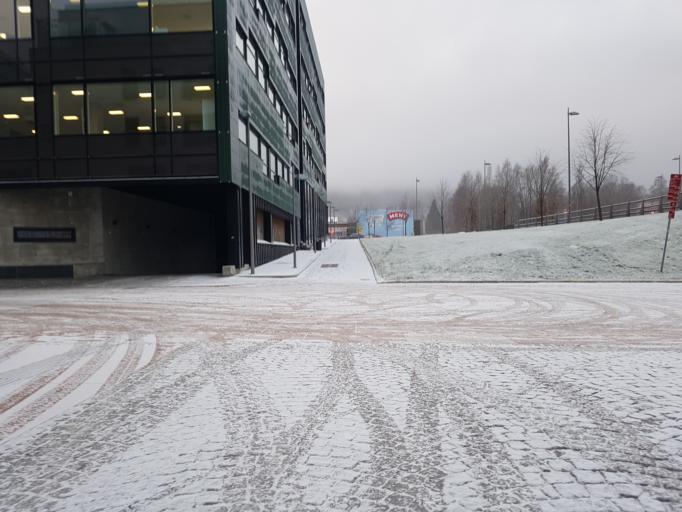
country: NO
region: Buskerud
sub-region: Drammen
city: Drammen
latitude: 59.7443
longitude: 10.1902
